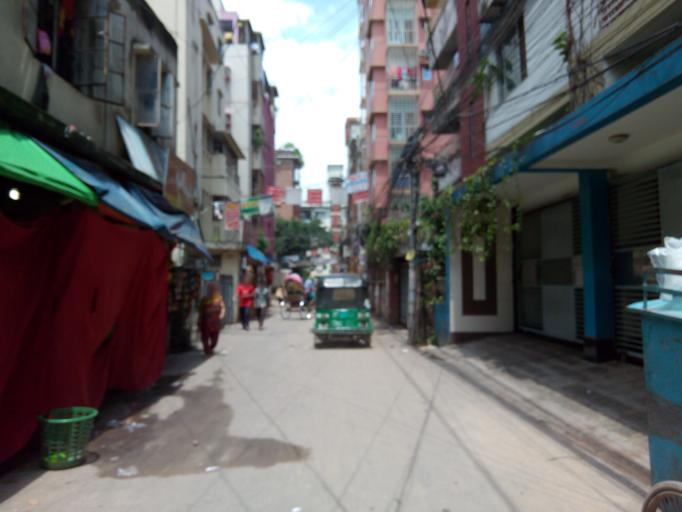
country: BD
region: Dhaka
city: Azimpur
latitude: 23.7477
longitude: 90.3832
